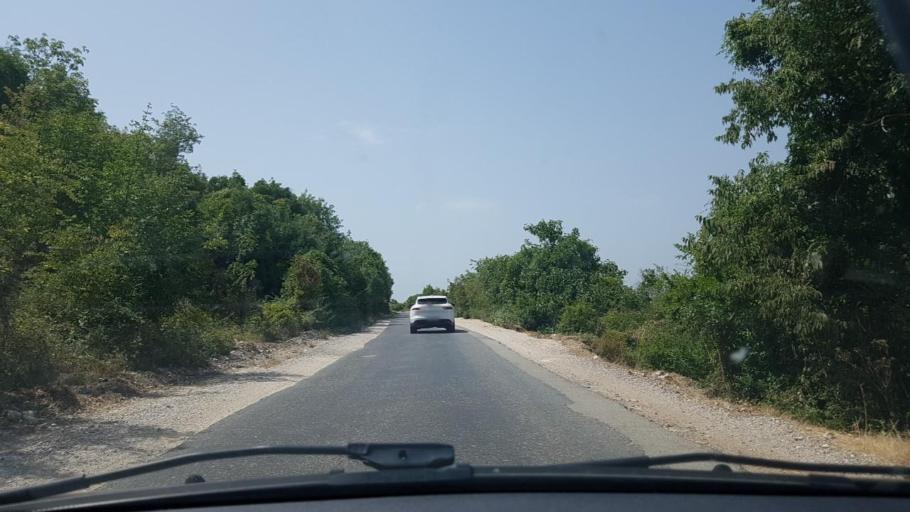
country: BA
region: Federation of Bosnia and Herzegovina
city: Tasovcici
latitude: 43.0267
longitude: 17.7539
